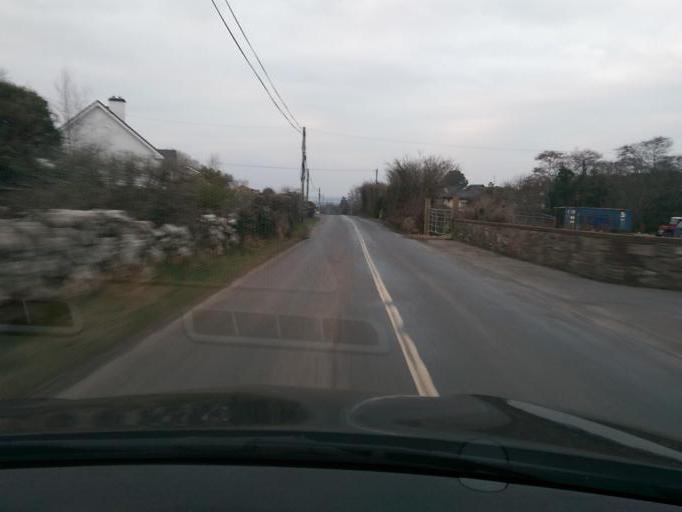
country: IE
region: Connaught
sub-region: County Galway
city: Moycullen
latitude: 53.3002
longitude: -9.1586
